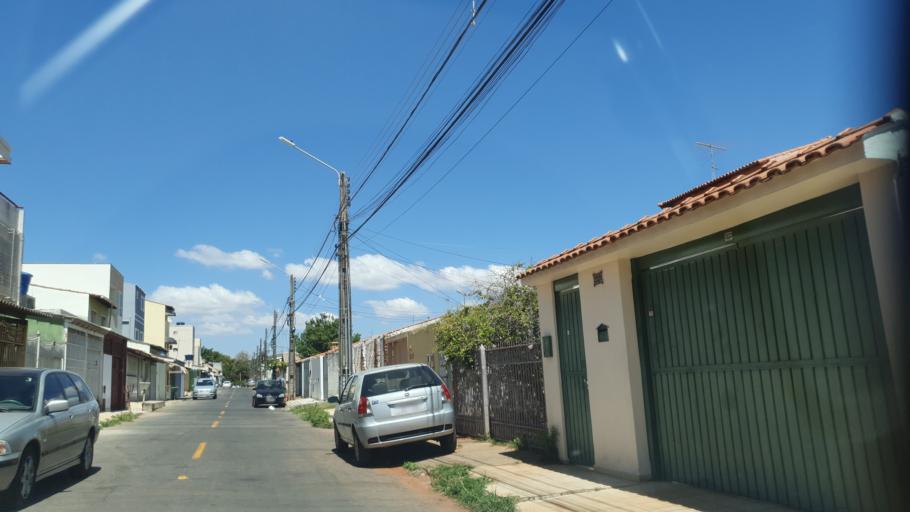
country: BR
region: Federal District
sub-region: Brasilia
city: Brasilia
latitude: -15.7890
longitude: -47.9380
